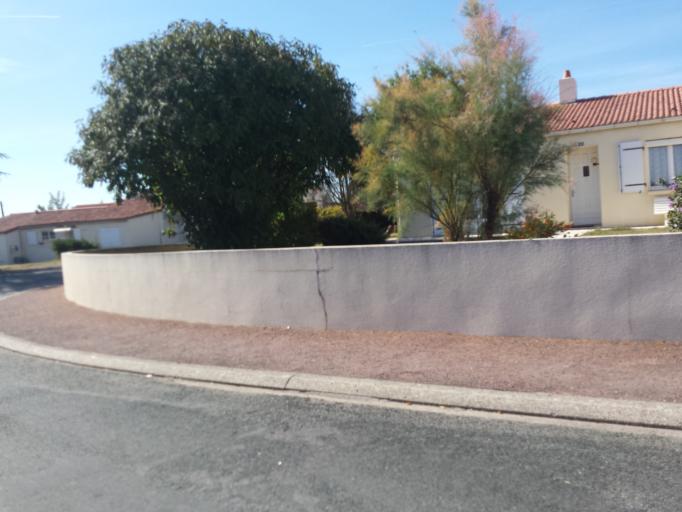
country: FR
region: Pays de la Loire
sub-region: Departement de la Vendee
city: La Chaize-le-Vicomte
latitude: 46.6736
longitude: -1.2887
